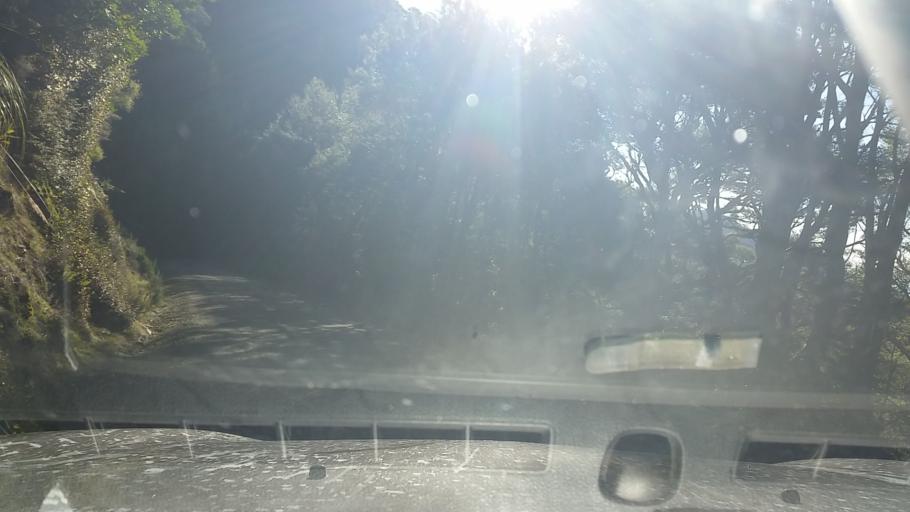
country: NZ
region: Marlborough
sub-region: Marlborough District
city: Picton
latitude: -41.0633
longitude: 174.1631
